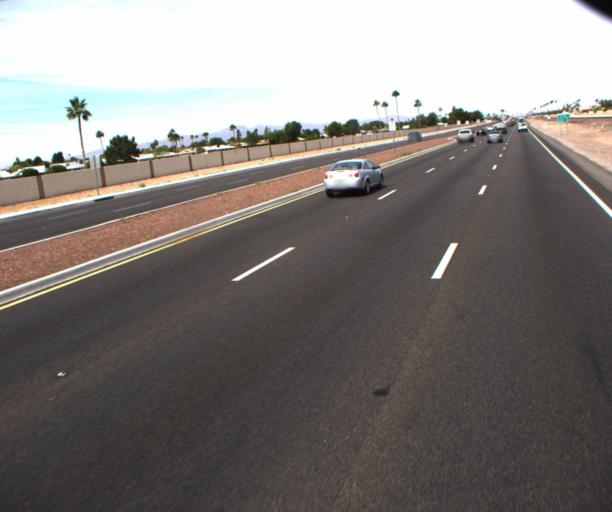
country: US
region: Arizona
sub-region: Maricopa County
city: Sun City
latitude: 33.5953
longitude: -112.2641
